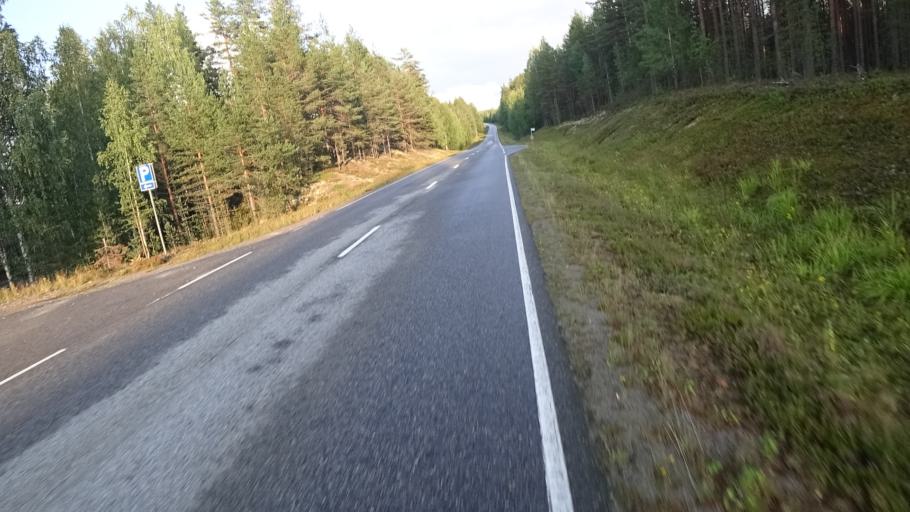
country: FI
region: North Karelia
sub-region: Joensuu
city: Ilomantsi
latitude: 62.6263
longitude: 31.1050
